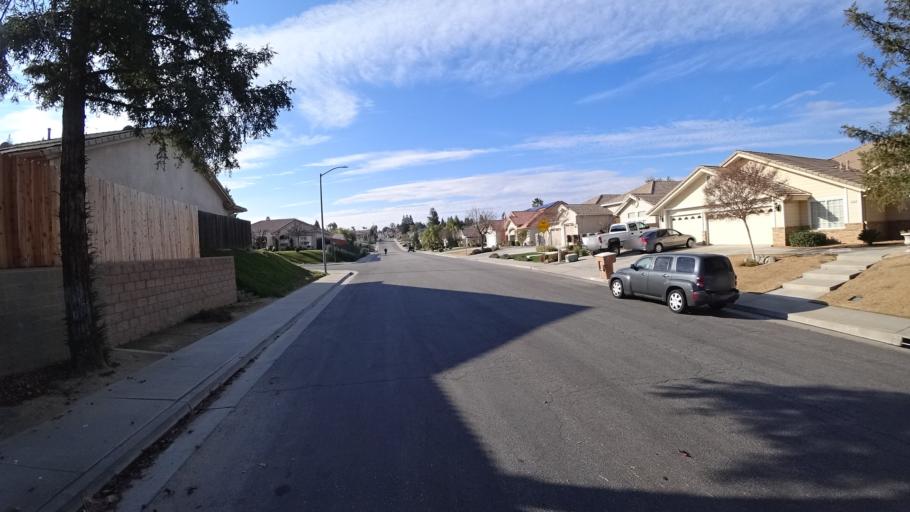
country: US
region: California
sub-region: Kern County
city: Oildale
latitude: 35.4012
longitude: -118.9145
